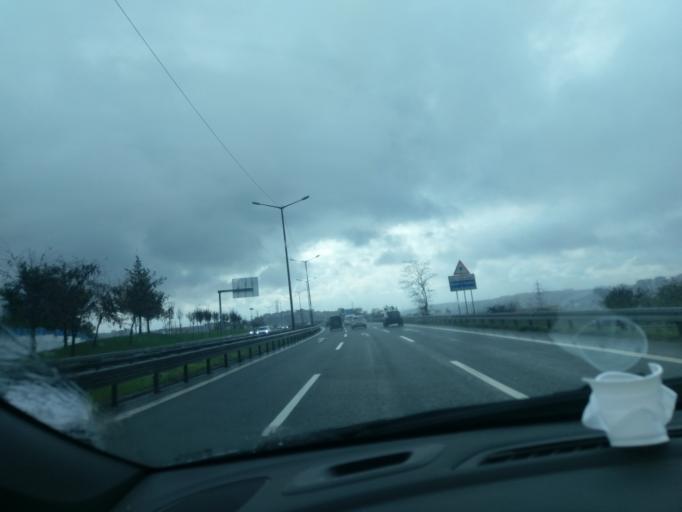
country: TR
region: Istanbul
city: Sisli
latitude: 41.0921
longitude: 28.9614
